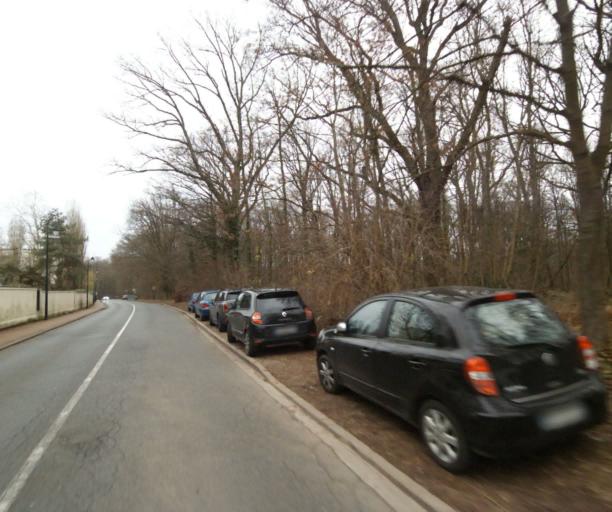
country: FR
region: Ile-de-France
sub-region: Departement des Hauts-de-Seine
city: Garches
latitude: 48.8484
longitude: 2.1735
